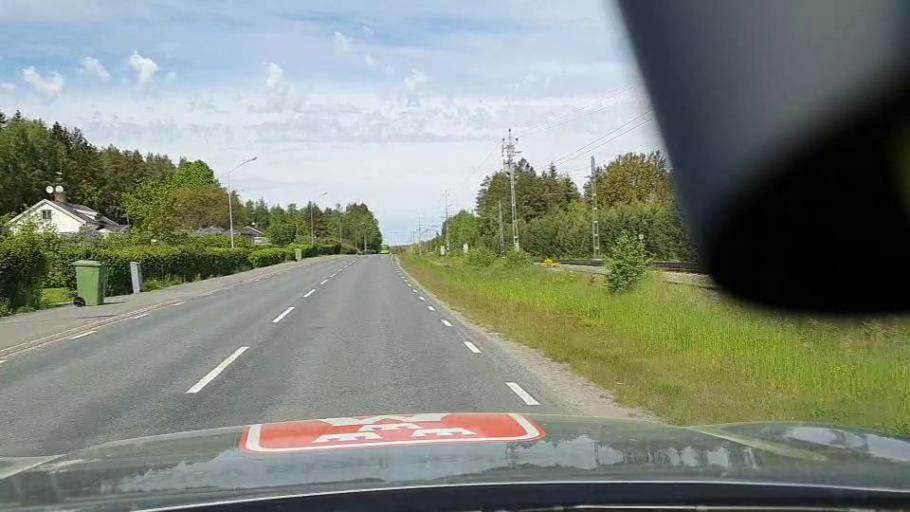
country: SE
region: Soedermanland
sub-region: Eskilstuna Kommun
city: Skogstorp
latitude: 59.2979
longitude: 16.4591
